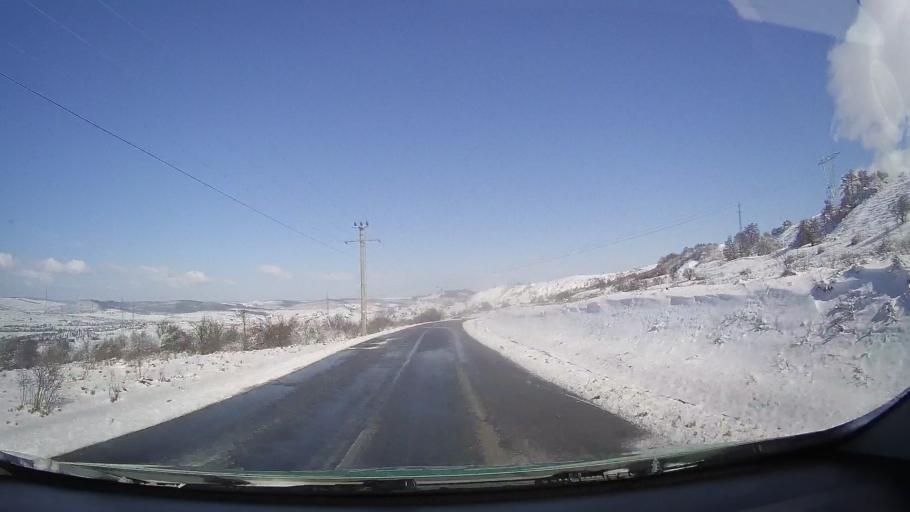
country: RO
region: Sibiu
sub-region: Comuna Avrig
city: Avrig
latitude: 45.7741
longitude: 24.3672
